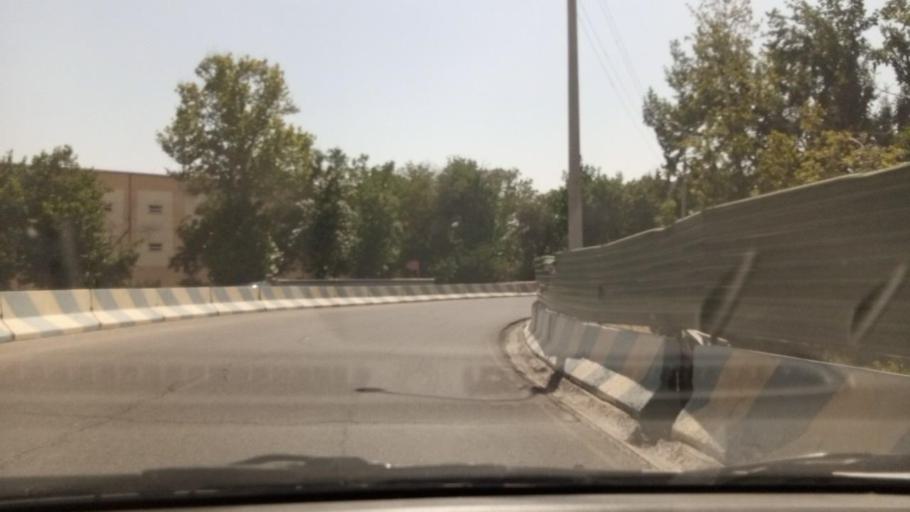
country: UZ
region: Toshkent Shahri
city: Tashkent
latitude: 41.2548
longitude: 69.1938
